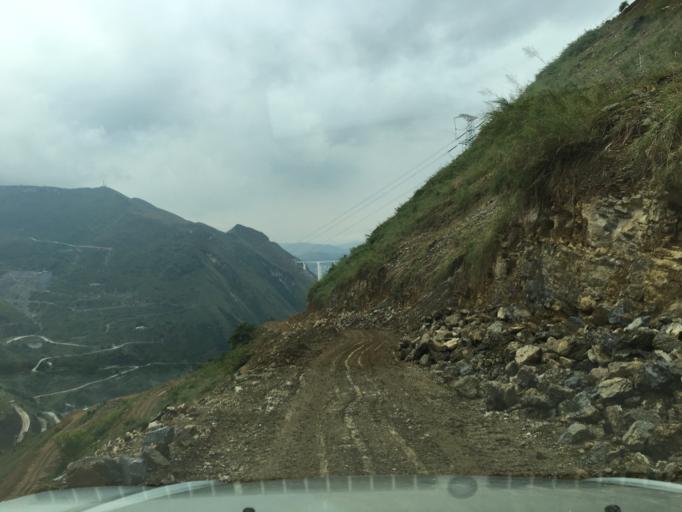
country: CN
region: Guizhou Sheng
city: Liupanshui
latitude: 25.9631
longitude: 105.2378
